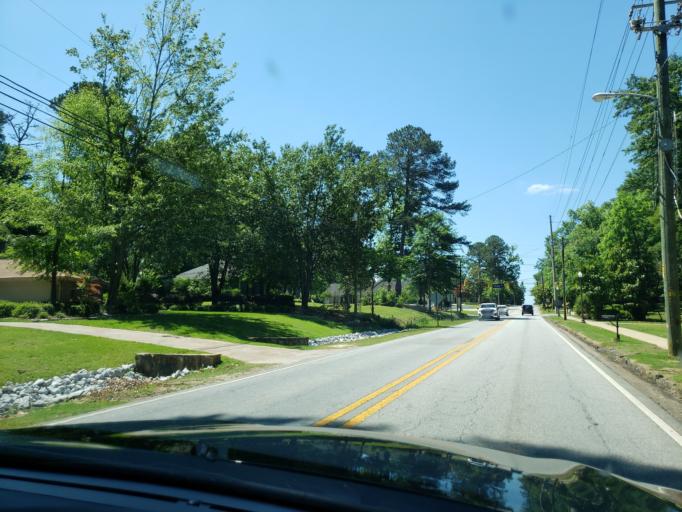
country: US
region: Alabama
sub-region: Lee County
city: Auburn
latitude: 32.6151
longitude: -85.4818
